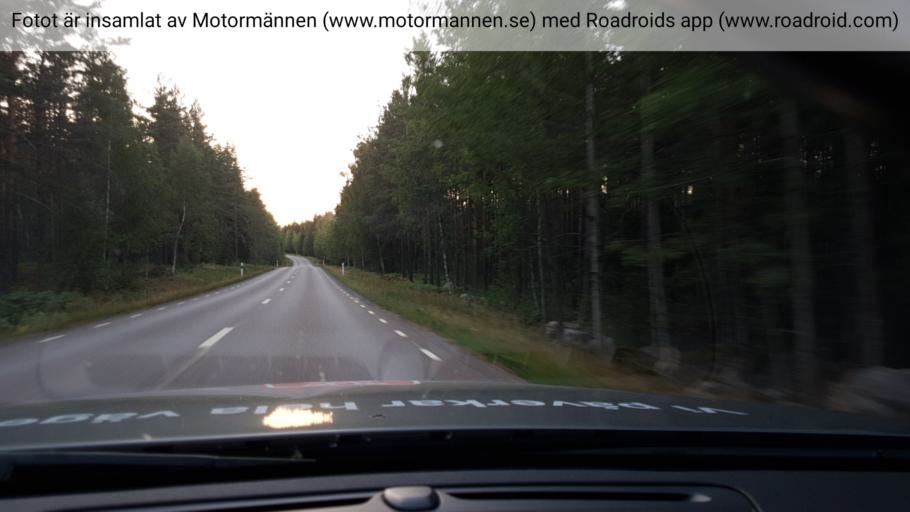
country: SE
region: Uppsala
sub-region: Heby Kommun
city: OEstervala
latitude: 60.0081
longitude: 17.2961
